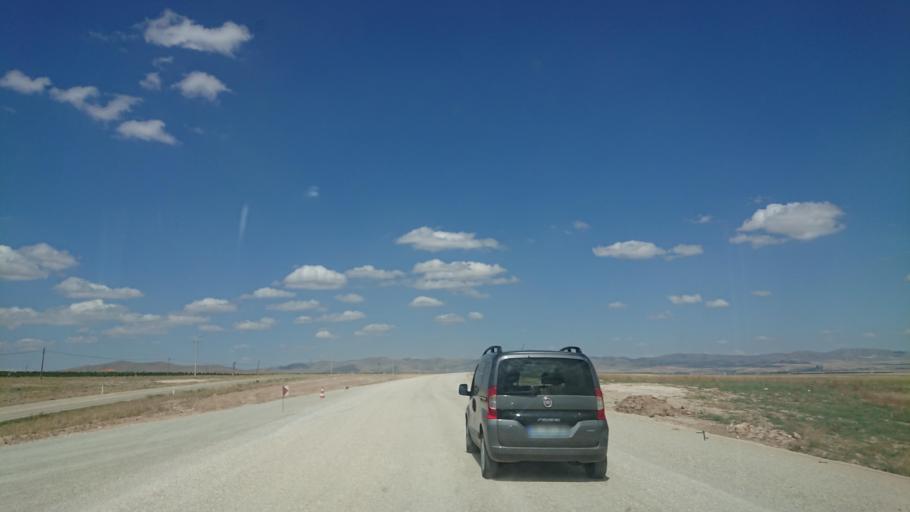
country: TR
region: Kirsehir
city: Kirsehir
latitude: 39.1334
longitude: 34.0451
